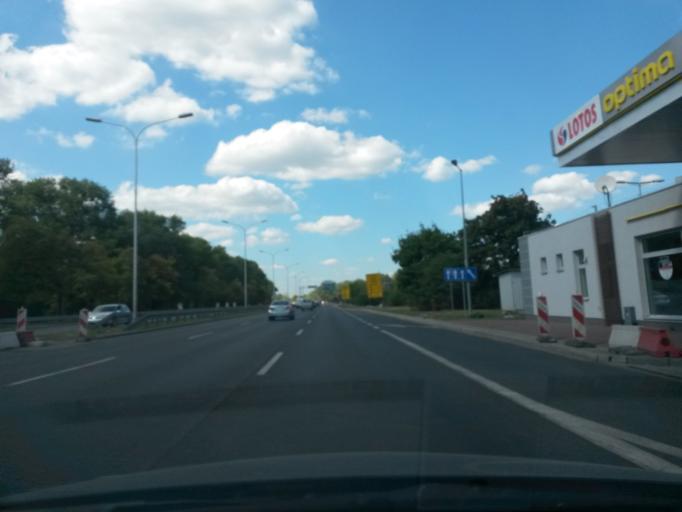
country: PL
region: Masovian Voivodeship
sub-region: Warszawa
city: Zoliborz
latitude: 52.2771
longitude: 20.9942
